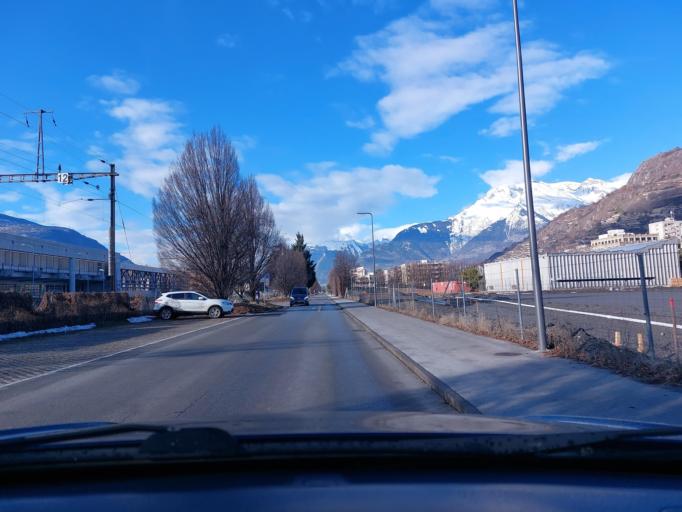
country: CH
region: Valais
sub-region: Sion District
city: Sitten
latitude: 46.2259
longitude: 7.3507
